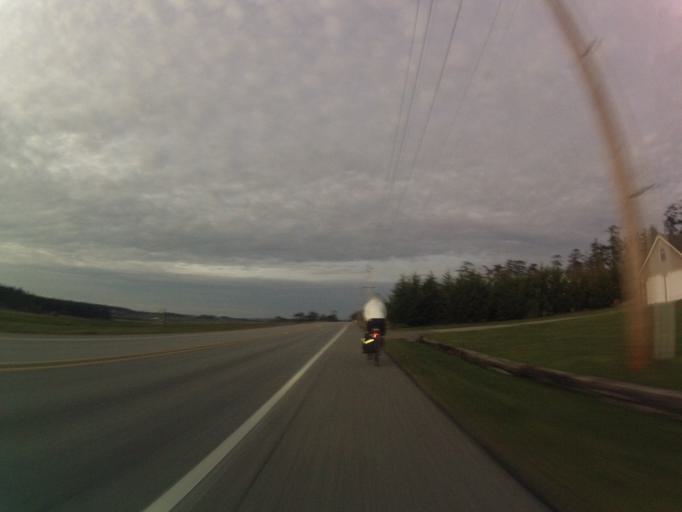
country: US
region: Washington
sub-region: Island County
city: Coupeville
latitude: 48.1834
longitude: -122.6880
